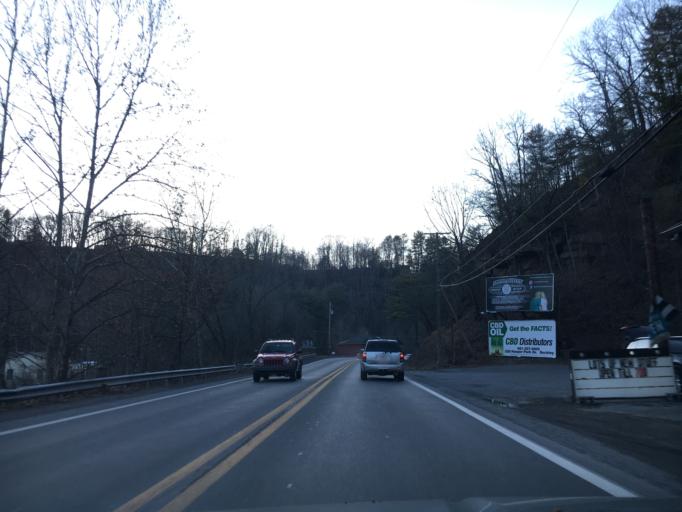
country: US
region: West Virginia
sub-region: Raleigh County
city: Beaver
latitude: 37.7512
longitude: -81.1457
